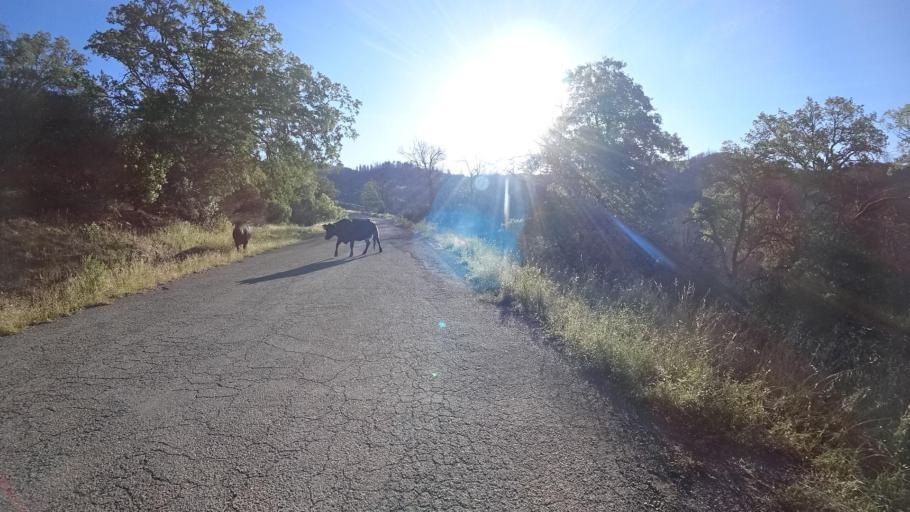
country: US
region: California
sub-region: Lake County
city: Upper Lake
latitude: 39.2639
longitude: -122.9288
